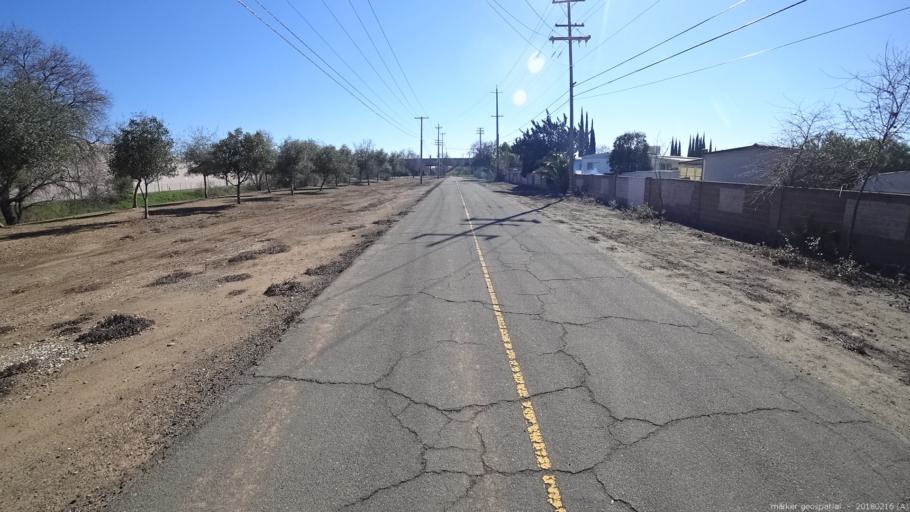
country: US
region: California
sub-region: Sacramento County
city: Gold River
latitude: 38.6135
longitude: -121.2651
